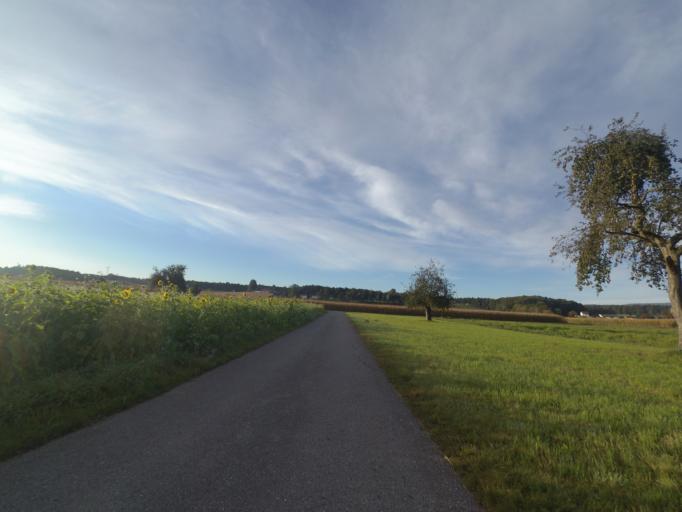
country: AT
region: Styria
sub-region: Politischer Bezirk Deutschlandsberg
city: Sankt Martin im Sulmtal
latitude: 46.7519
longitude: 15.2908
